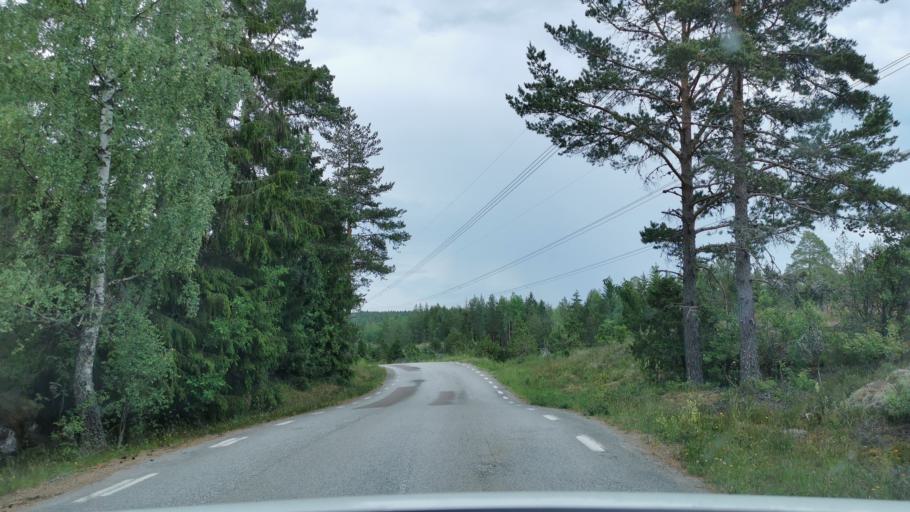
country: SE
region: Vaestra Goetaland
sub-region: Bengtsfors Kommun
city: Dals Langed
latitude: 58.8711
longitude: 12.4036
